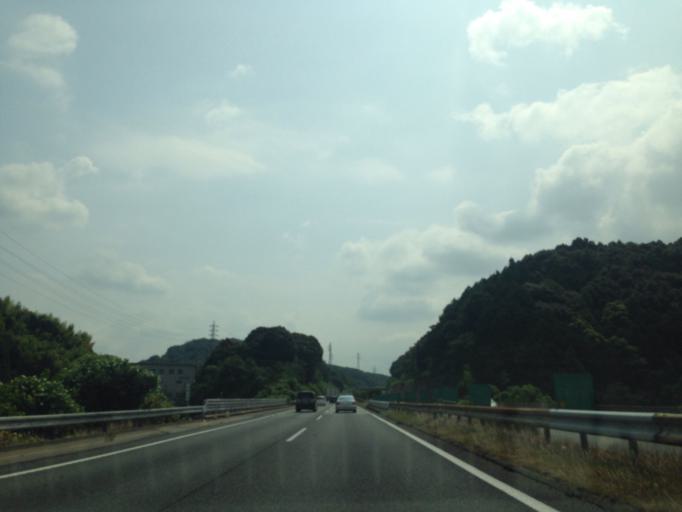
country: JP
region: Aichi
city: Kozakai-cho
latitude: 34.8622
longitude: 137.3162
